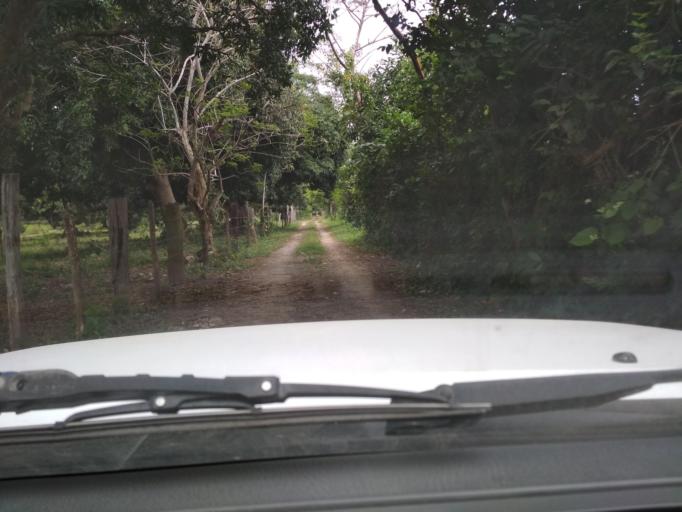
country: MX
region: Veracruz
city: El Tejar
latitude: 19.0745
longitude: -96.1466
